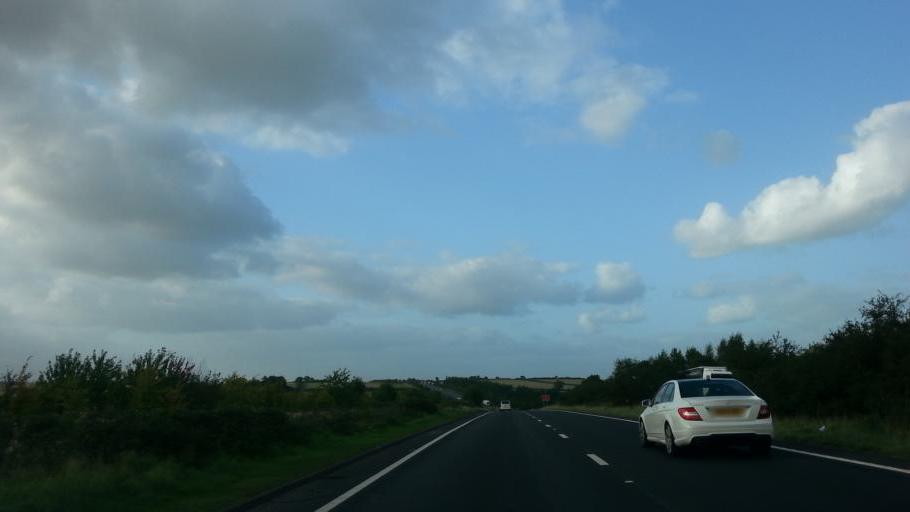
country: GB
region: England
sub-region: Hampshire
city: Overton
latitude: 51.1950
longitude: -1.3369
